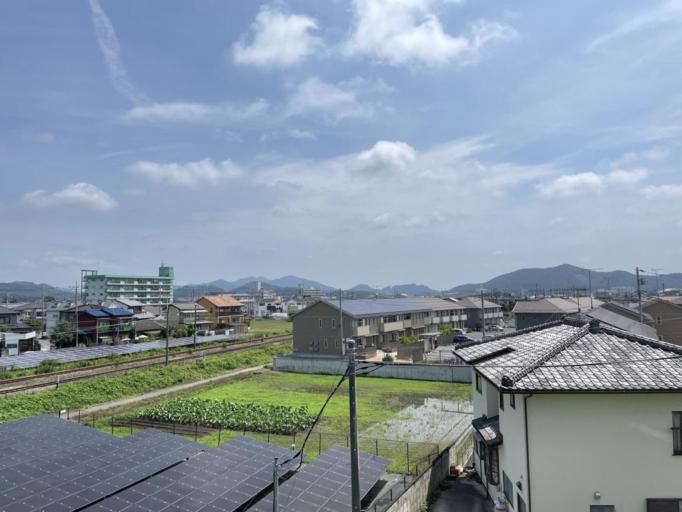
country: JP
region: Tochigi
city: Sano
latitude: 36.3165
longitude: 139.5872
